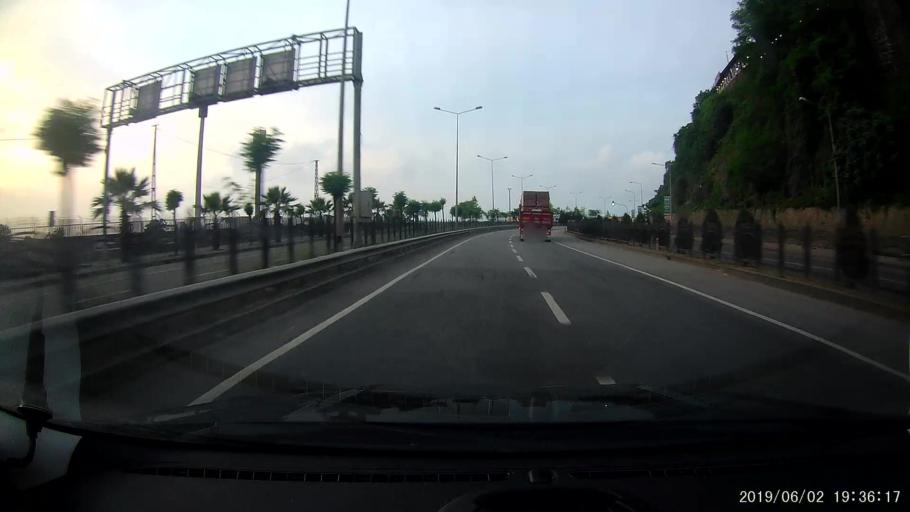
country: TR
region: Giresun
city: Giresun
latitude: 40.9220
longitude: 38.3866
